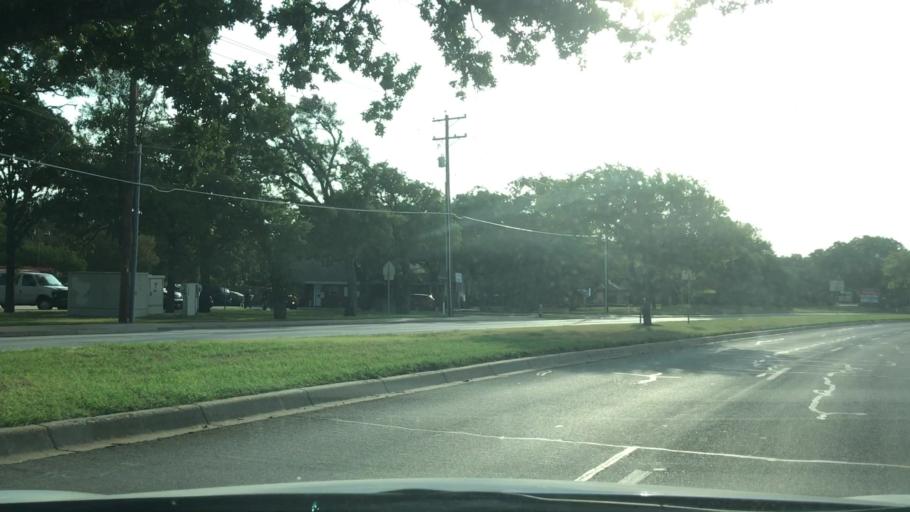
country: US
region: Texas
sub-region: Tarrant County
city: Arlington
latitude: 32.7647
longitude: -97.1228
